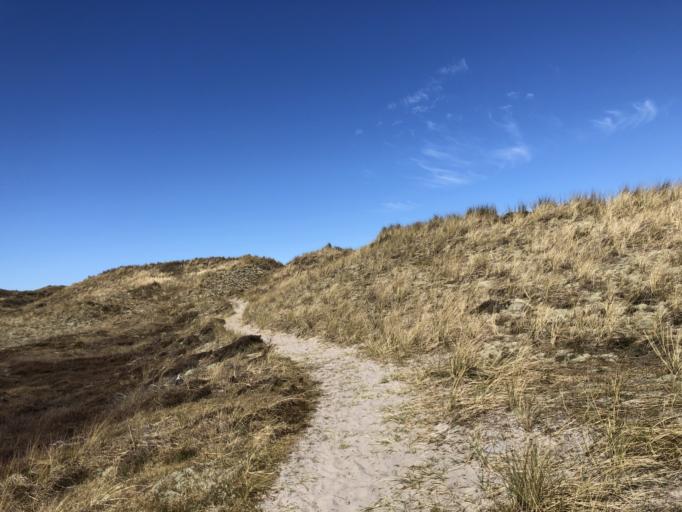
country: DK
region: Central Jutland
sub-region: Holstebro Kommune
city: Ulfborg
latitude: 56.3048
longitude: 8.1286
